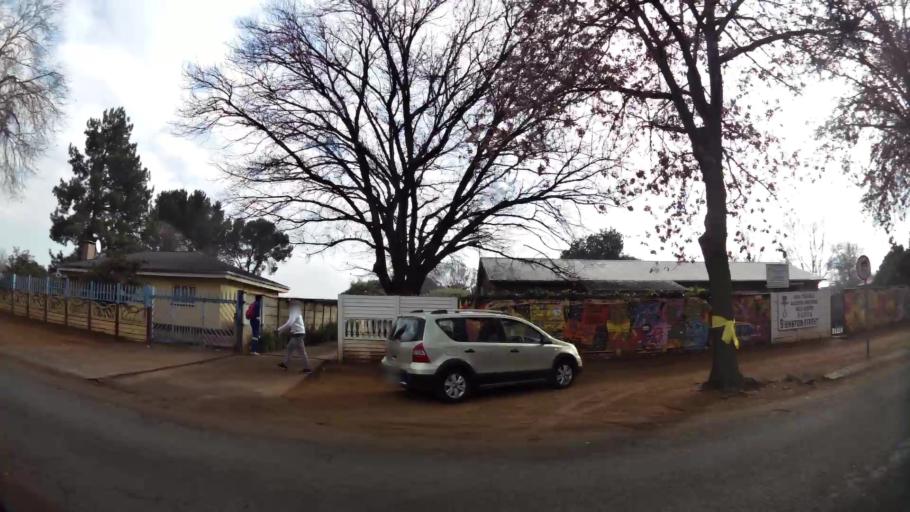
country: ZA
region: Gauteng
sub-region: Sedibeng District Municipality
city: Vanderbijlpark
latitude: -26.6952
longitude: 27.8234
